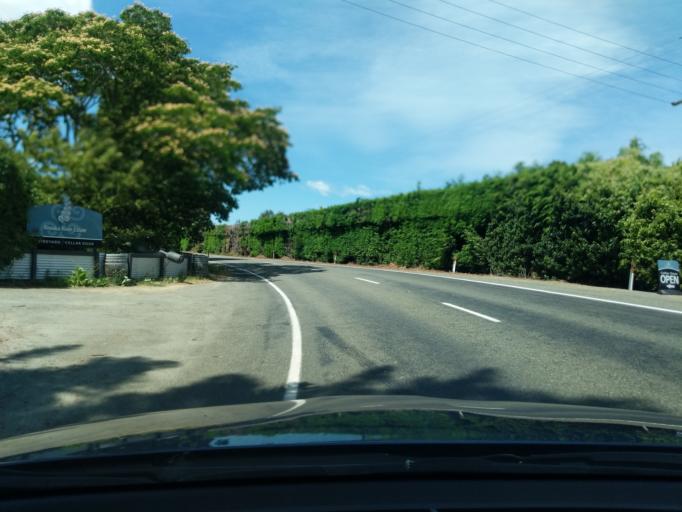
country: NZ
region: Tasman
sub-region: Tasman District
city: Motueka
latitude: -41.0626
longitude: 172.9779
